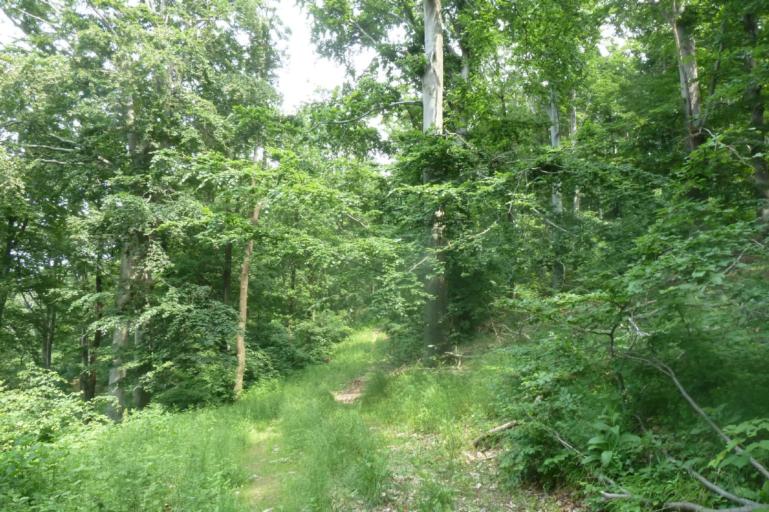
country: HU
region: Pest
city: Csobanka
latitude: 47.6945
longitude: 18.9616
